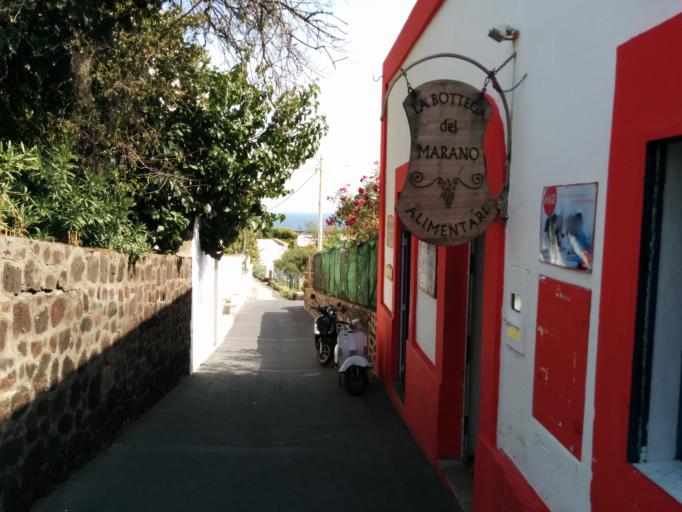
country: IT
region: Sicily
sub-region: Messina
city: Canneto
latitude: 38.8043
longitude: 15.2350
